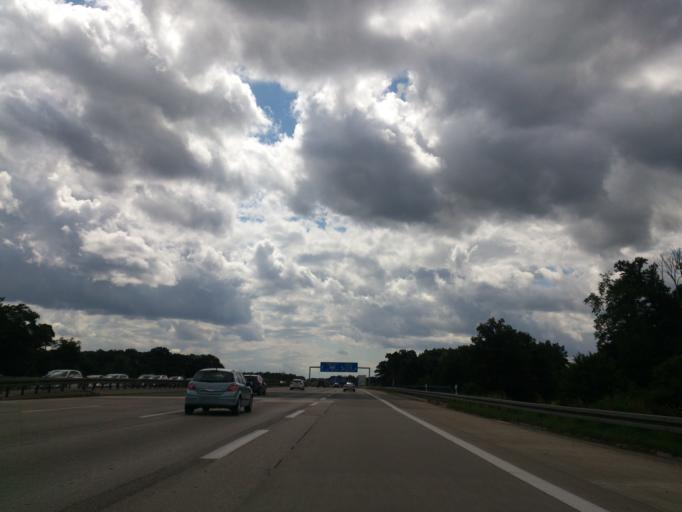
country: DE
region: Lower Saxony
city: Elze
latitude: 52.5526
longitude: 9.7936
